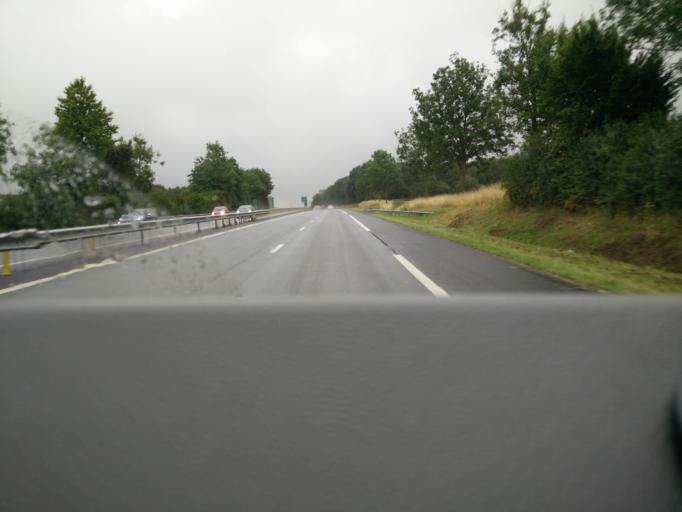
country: FR
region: Nord-Pas-de-Calais
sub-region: Departement du Pas-de-Calais
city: Saint-Pol-sur-Ternoise
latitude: 50.3631
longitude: 2.3932
